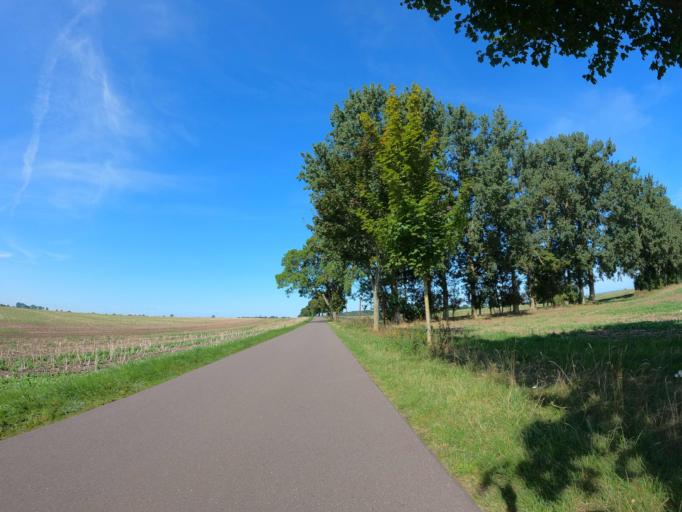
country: DE
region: Mecklenburg-Vorpommern
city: Kramerhof
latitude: 54.3617
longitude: 13.0604
